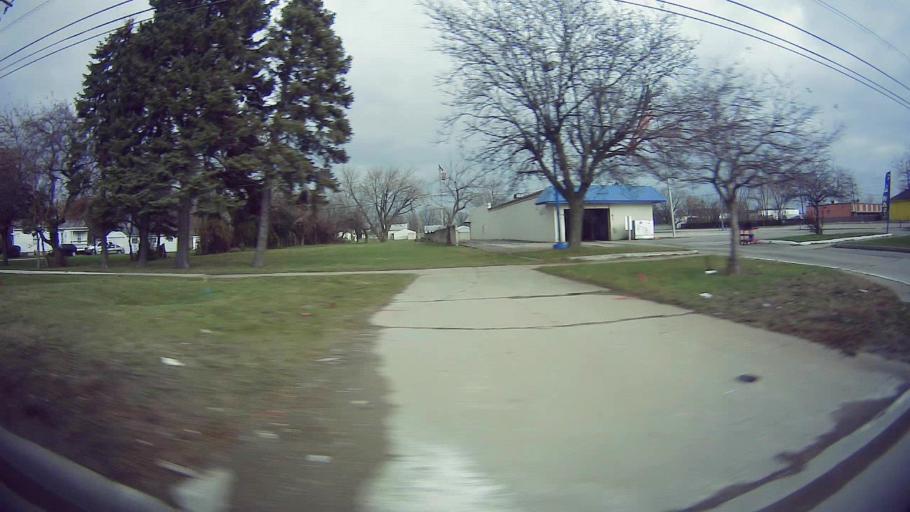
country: US
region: Michigan
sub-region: Macomb County
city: Eastpointe
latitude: 42.4796
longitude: -82.9867
